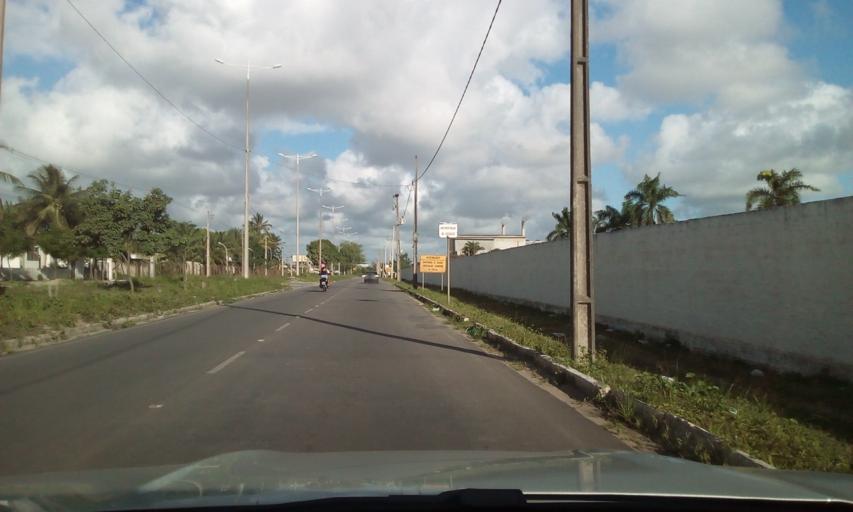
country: BR
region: Paraiba
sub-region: Bayeux
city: Bayeux
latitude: -7.1773
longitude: -34.9108
